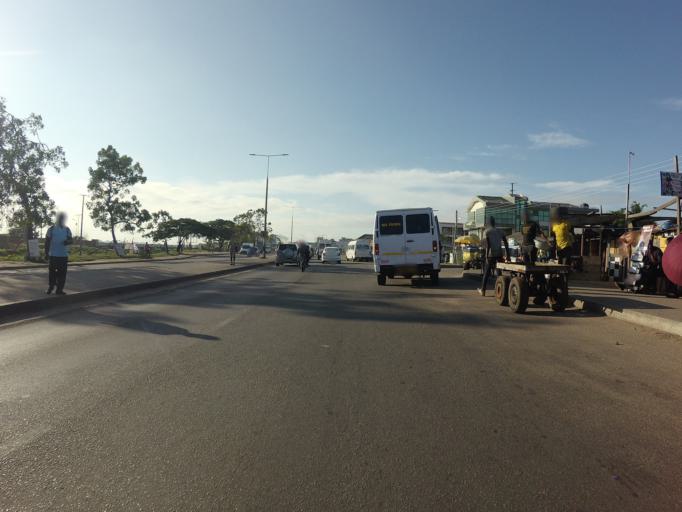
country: GH
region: Greater Accra
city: Accra
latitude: 5.5543
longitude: -0.2316
